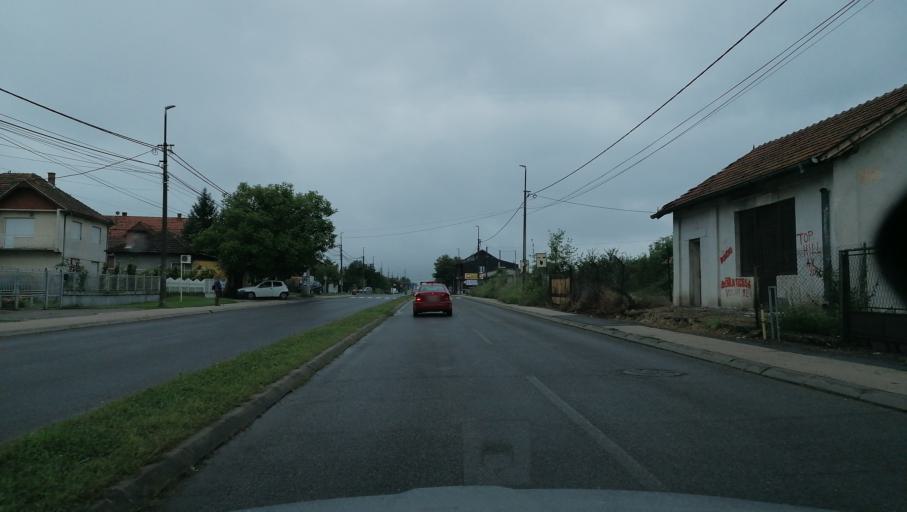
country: RS
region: Central Serbia
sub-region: Rasinski Okrug
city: Krusevac
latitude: 43.5861
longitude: 21.2941
